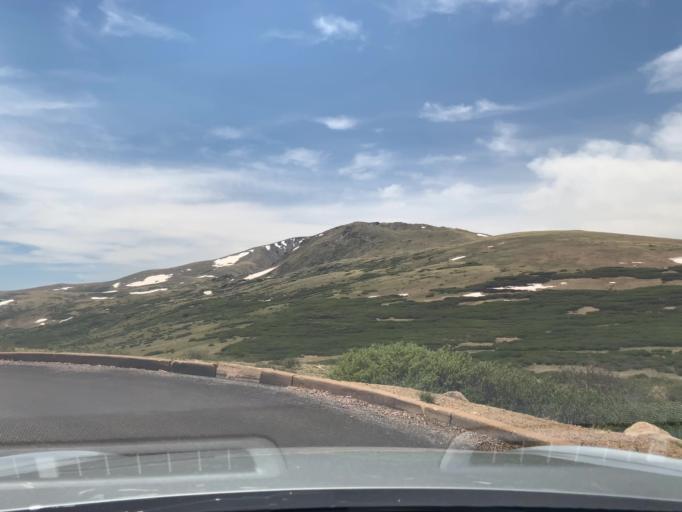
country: US
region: Colorado
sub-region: Clear Creek County
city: Georgetown
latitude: 39.5974
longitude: -105.7129
